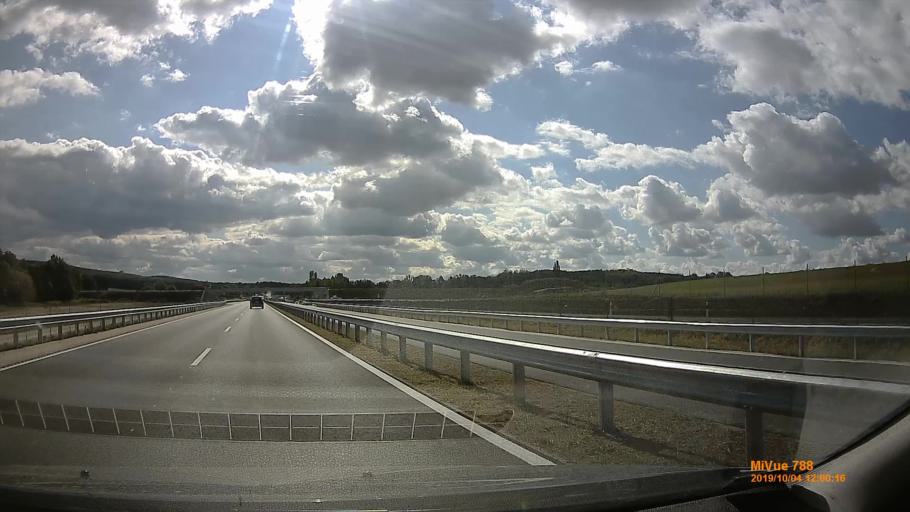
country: HU
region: Somogy
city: Karad
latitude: 46.6273
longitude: 17.7941
